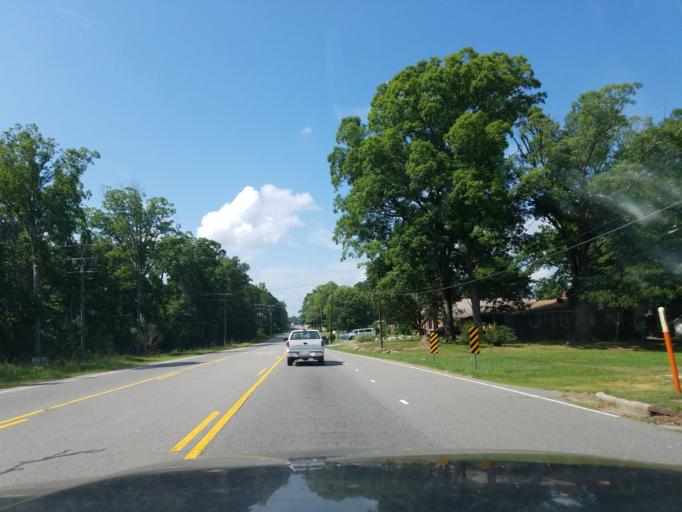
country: US
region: North Carolina
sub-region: Durham County
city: Durham
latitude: 35.9471
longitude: -78.9039
